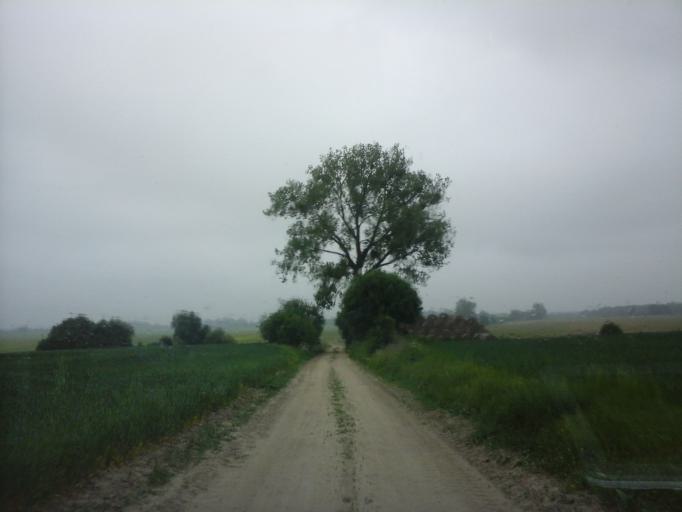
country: PL
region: West Pomeranian Voivodeship
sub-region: Powiat choszczenski
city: Pelczyce
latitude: 53.0729
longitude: 15.3404
